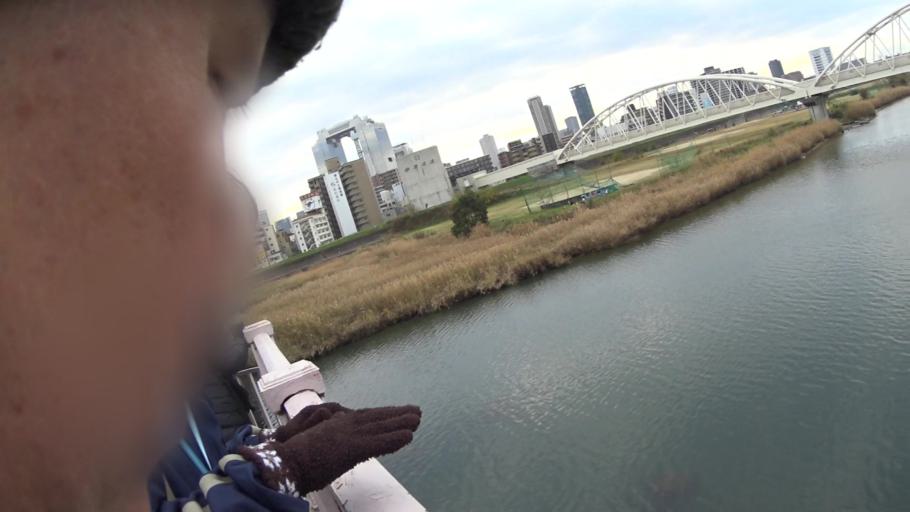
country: JP
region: Osaka
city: Osaka-shi
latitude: 34.7129
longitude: 135.4870
